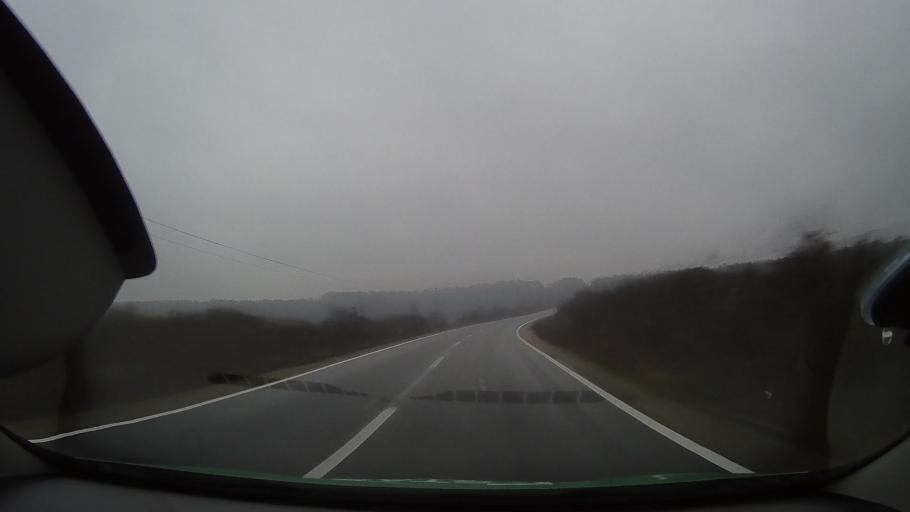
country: RO
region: Bihor
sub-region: Comuna Olcea
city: Olcea
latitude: 46.7061
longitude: 21.9624
